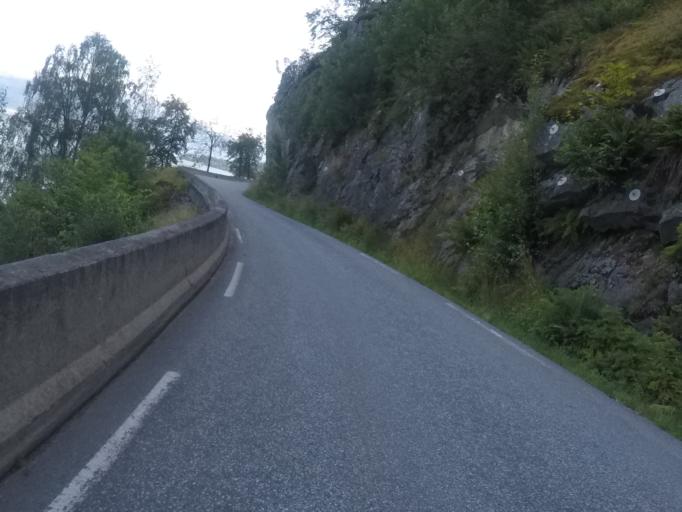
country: NO
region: Sogn og Fjordane
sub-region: Balestrand
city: Balestrand
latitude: 61.2379
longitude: 6.5514
